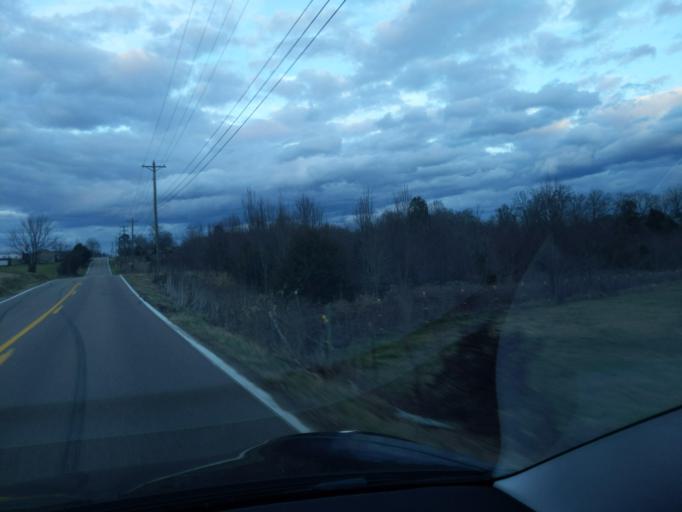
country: US
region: Tennessee
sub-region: Jefferson County
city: White Pine
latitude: 36.0911
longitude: -83.3618
